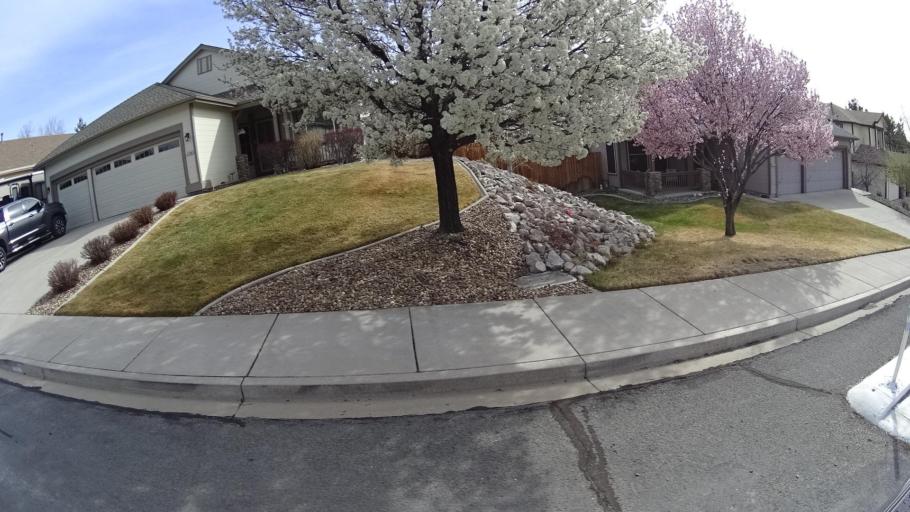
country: US
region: Nevada
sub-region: Washoe County
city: Mogul
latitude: 39.5429
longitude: -119.8963
